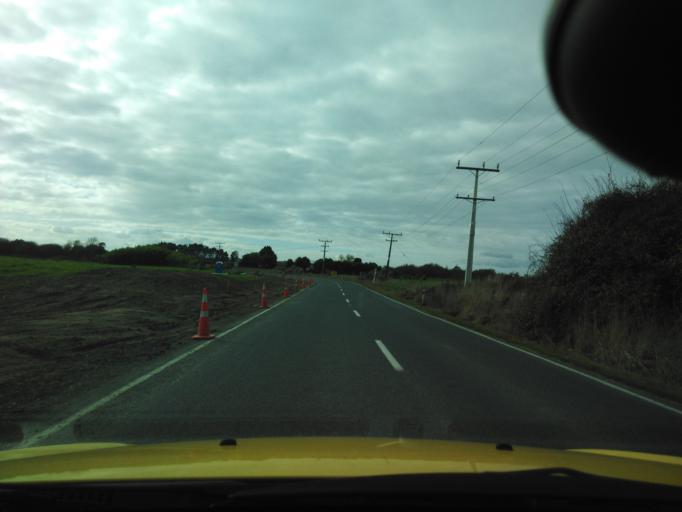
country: NZ
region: Waikato
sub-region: Waikato District
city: Te Kauwhata
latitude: -37.4750
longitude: 175.1449
